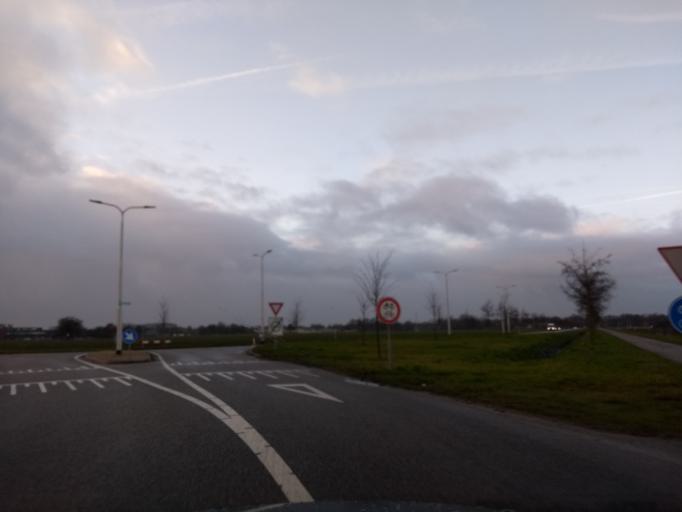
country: NL
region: Overijssel
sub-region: Gemeente Twenterand
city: Vriezenveen
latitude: 52.4073
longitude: 6.6478
